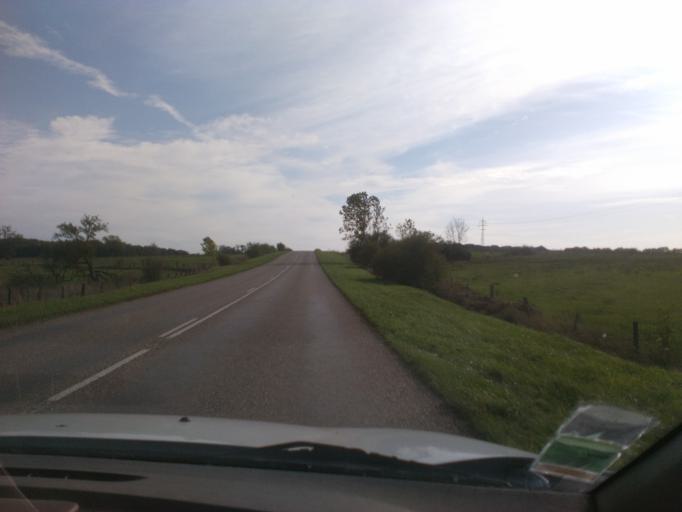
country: FR
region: Lorraine
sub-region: Departement des Vosges
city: Chatel-sur-Moselle
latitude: 48.3460
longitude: 6.4390
